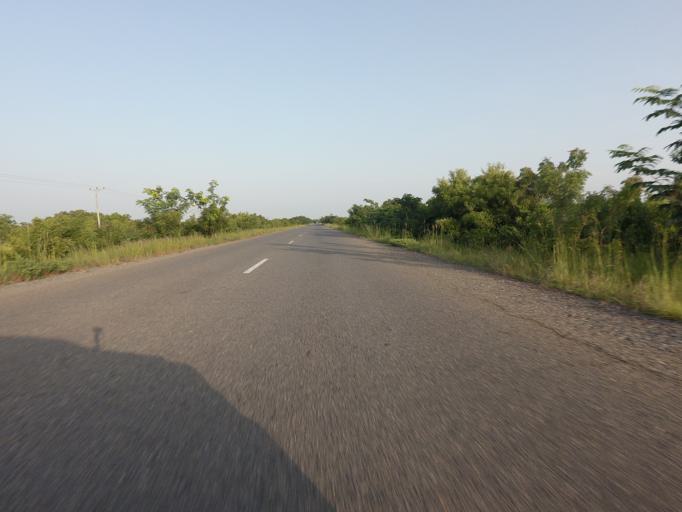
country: GH
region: Volta
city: Anloga
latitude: 5.9572
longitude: 0.6687
